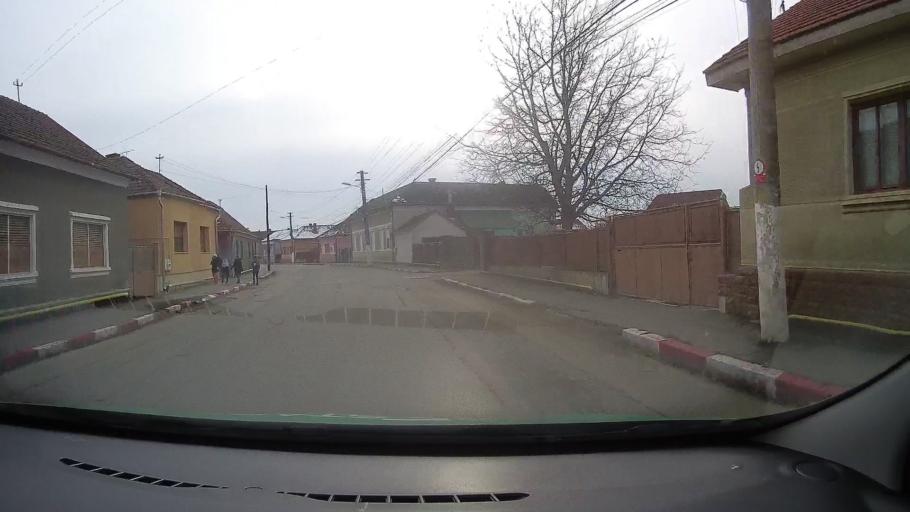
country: RO
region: Hunedoara
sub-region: Comuna Geoagiu
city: Geoagiu
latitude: 45.9228
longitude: 23.1992
